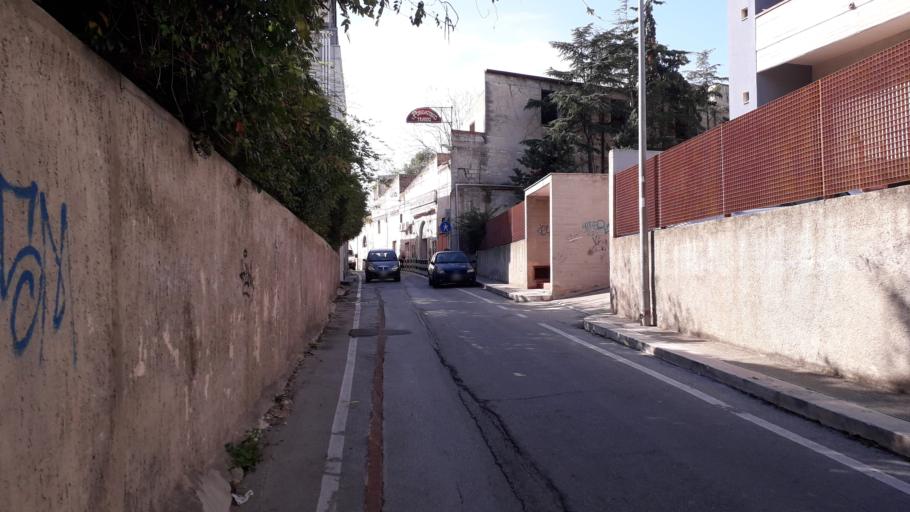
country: IT
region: Apulia
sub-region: Provincia di Bari
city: Bari
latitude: 41.1160
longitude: 16.8587
